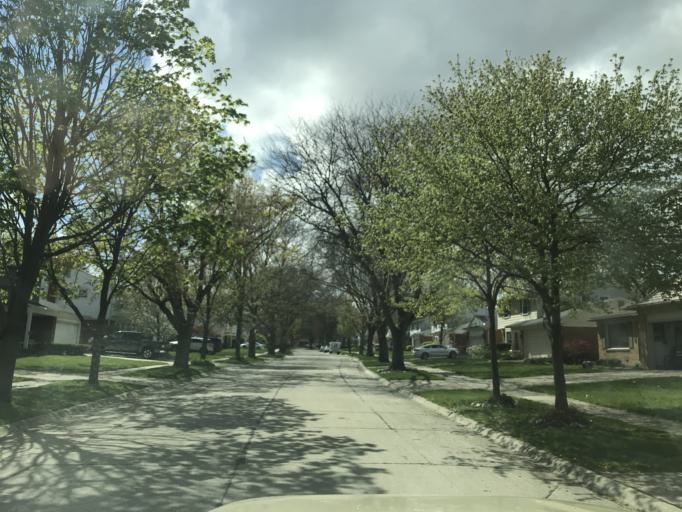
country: US
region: Michigan
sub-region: Wayne County
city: Plymouth
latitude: 42.3789
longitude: -83.4827
